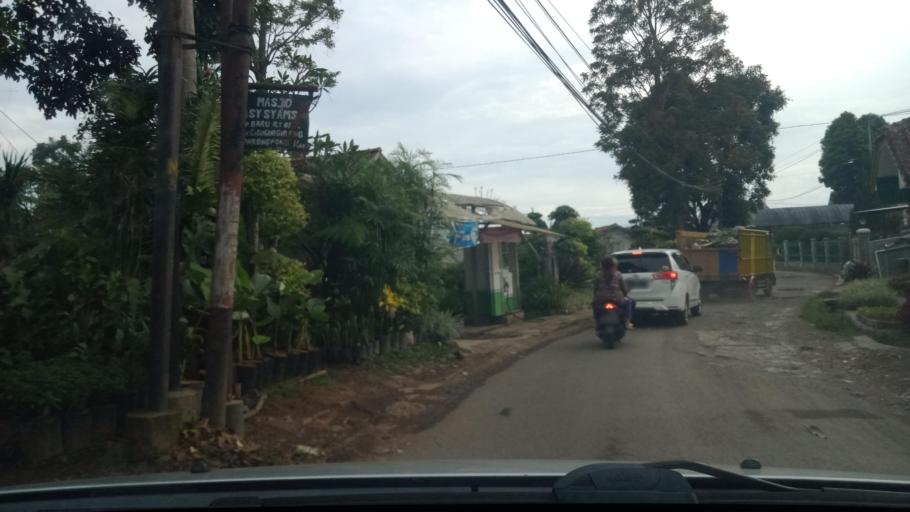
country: ID
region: West Java
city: Lembang
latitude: -6.8107
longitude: 107.5879
